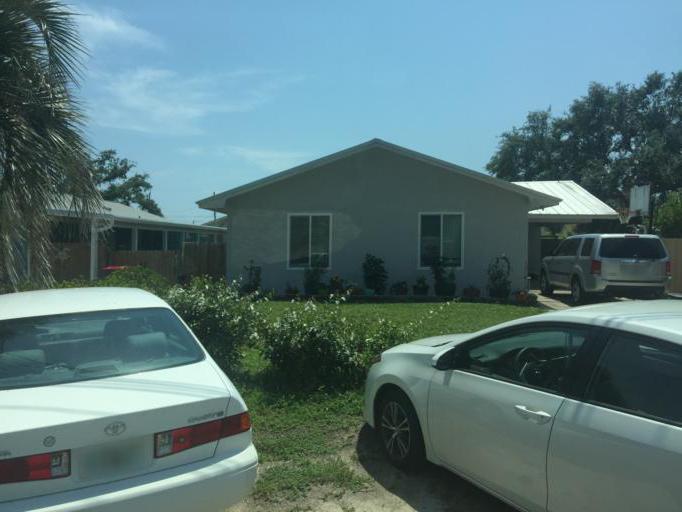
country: US
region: Florida
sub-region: Bay County
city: Lower Grand Lagoon
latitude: 30.1498
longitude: -85.7581
